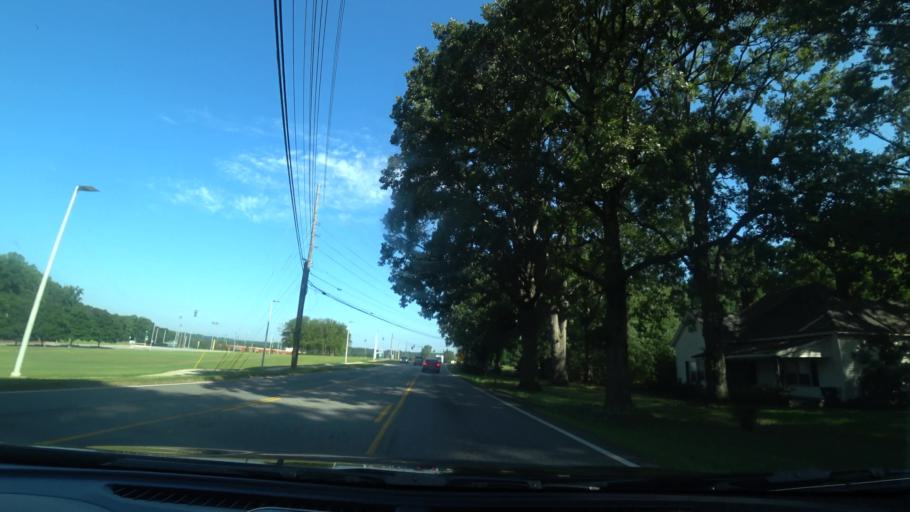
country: US
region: Georgia
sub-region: Gwinnett County
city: Lawrenceville
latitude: 33.9823
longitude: -83.9995
